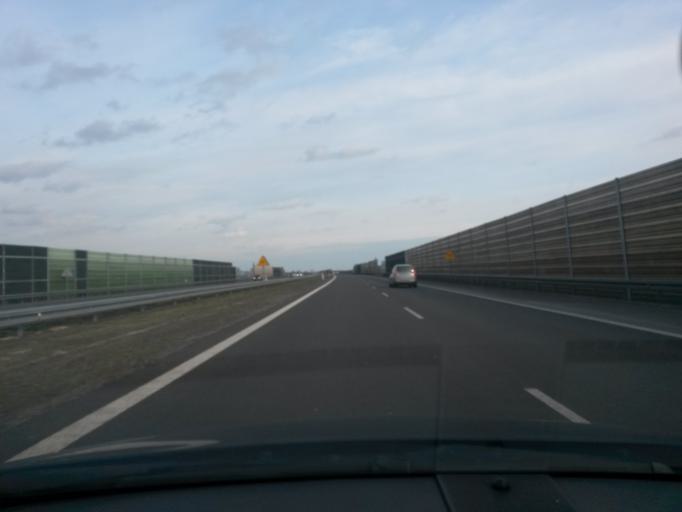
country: PL
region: Greater Poland Voivodeship
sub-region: Powiat turecki
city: Brudzew
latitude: 52.1233
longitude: 18.6826
